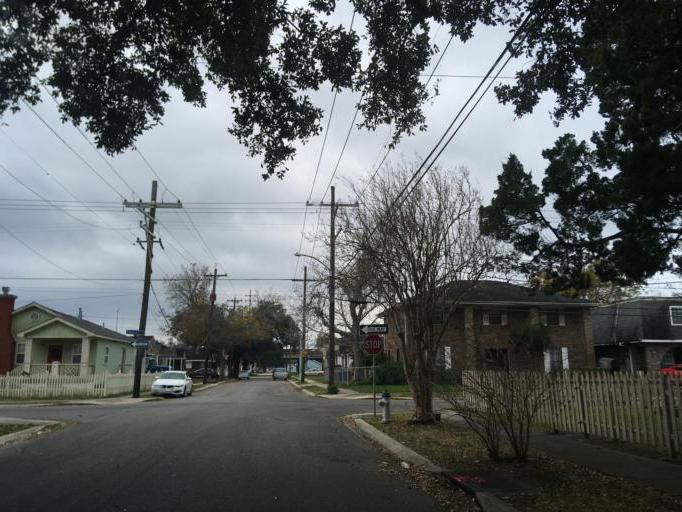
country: US
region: Louisiana
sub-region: Orleans Parish
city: New Orleans
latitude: 29.9930
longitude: -90.0612
